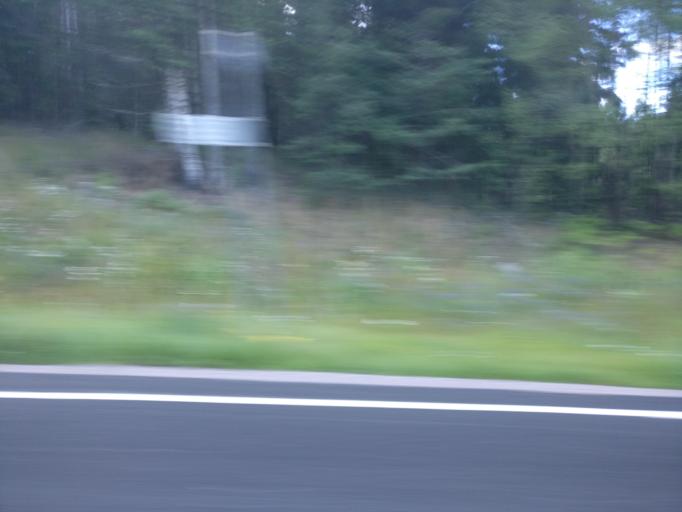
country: FI
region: Uusimaa
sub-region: Helsinki
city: Nurmijaervi
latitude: 60.4887
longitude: 24.5818
